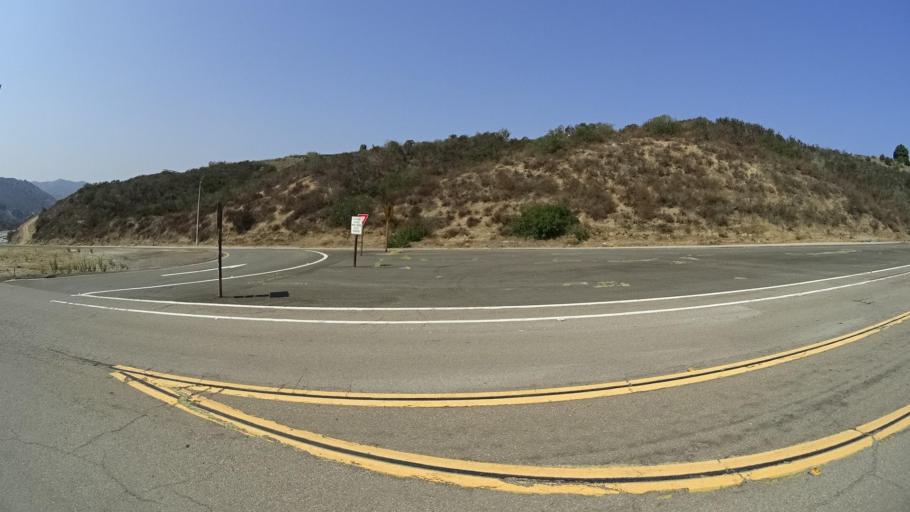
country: US
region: California
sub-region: San Diego County
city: Hidden Meadows
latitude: 33.2879
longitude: -117.1505
